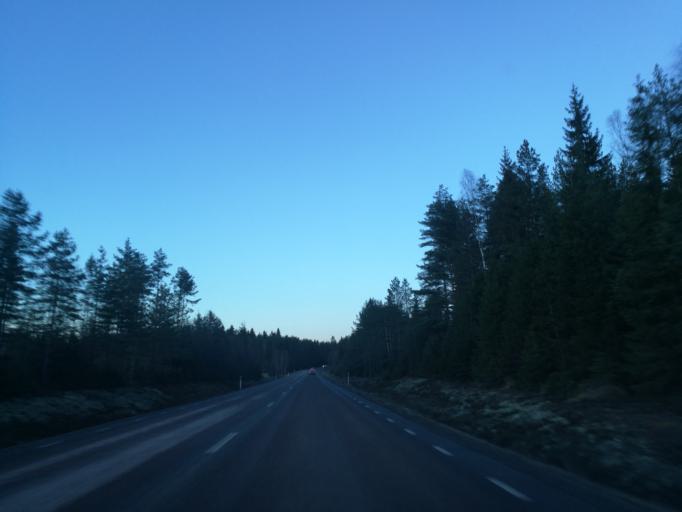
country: SE
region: Vaermland
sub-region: Eda Kommun
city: Charlottenberg
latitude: 59.8942
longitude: 12.2795
